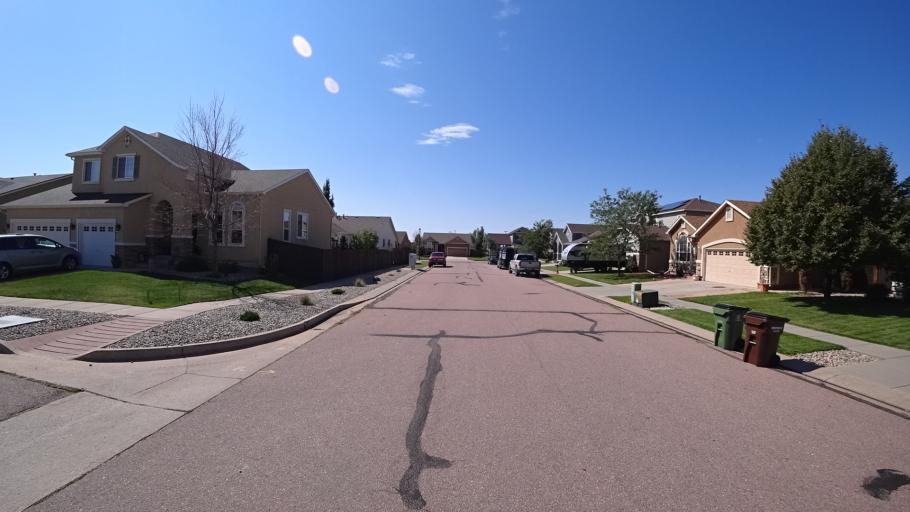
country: US
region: Colorado
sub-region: El Paso County
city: Cimarron Hills
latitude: 38.9234
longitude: -104.6993
